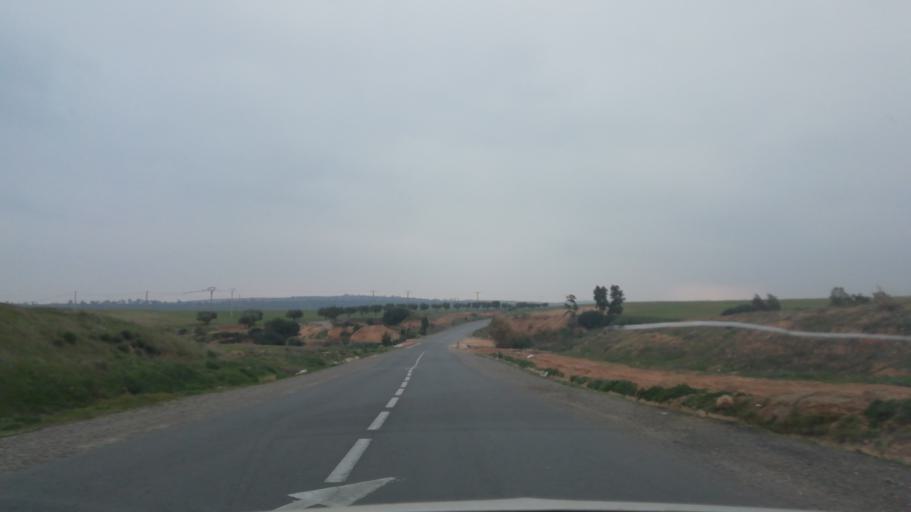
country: DZ
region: Sidi Bel Abbes
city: Sfizef
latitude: 35.2748
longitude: -0.1552
